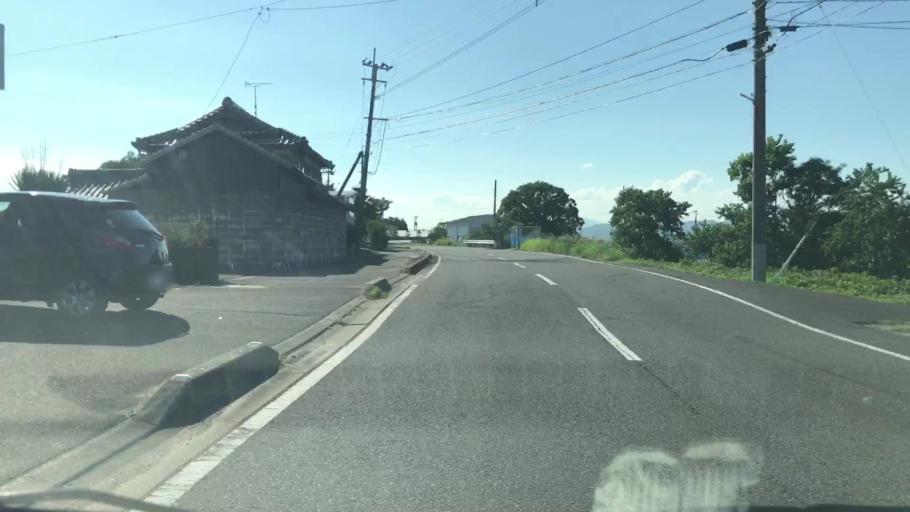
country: JP
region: Saga Prefecture
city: Saga-shi
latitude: 33.1907
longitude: 130.2850
